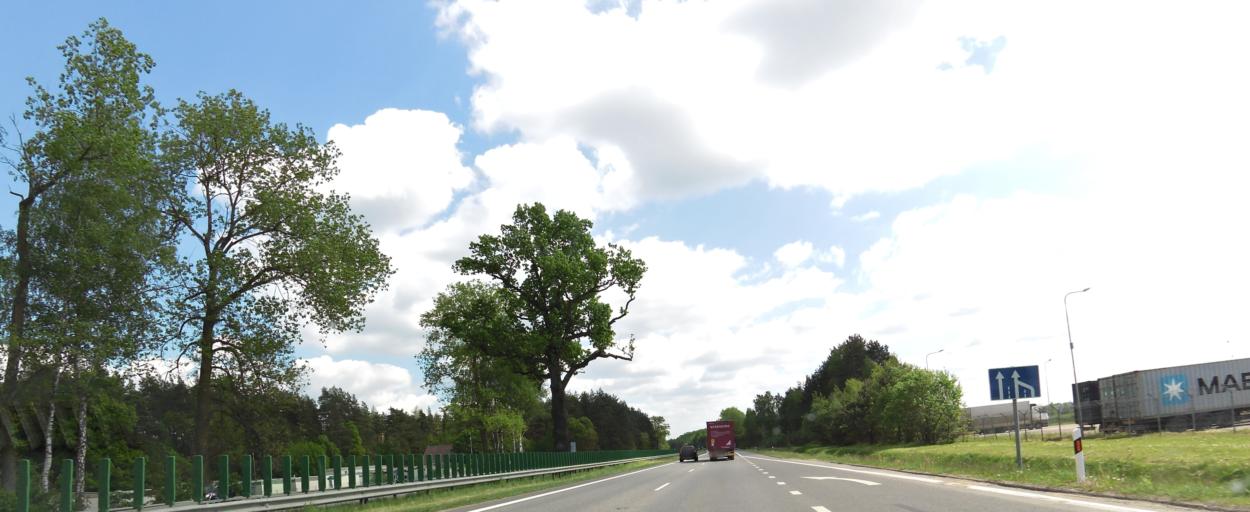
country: LT
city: Lentvaris
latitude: 54.7012
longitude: 25.0104
